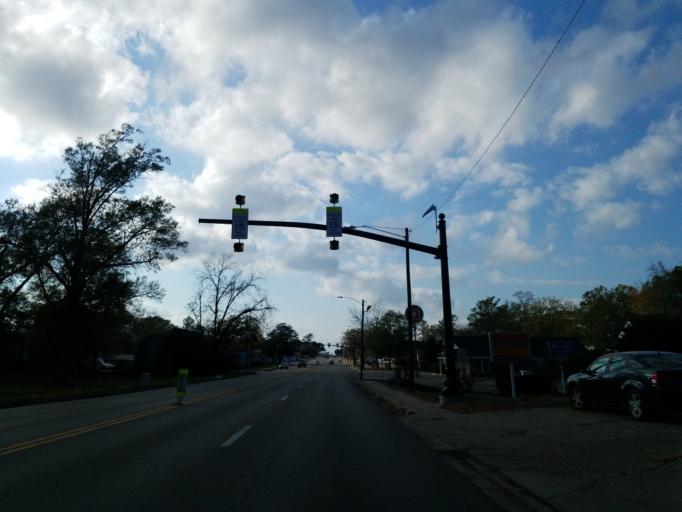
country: US
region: Mississippi
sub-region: Forrest County
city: Hattiesburg
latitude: 31.3248
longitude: -89.3210
